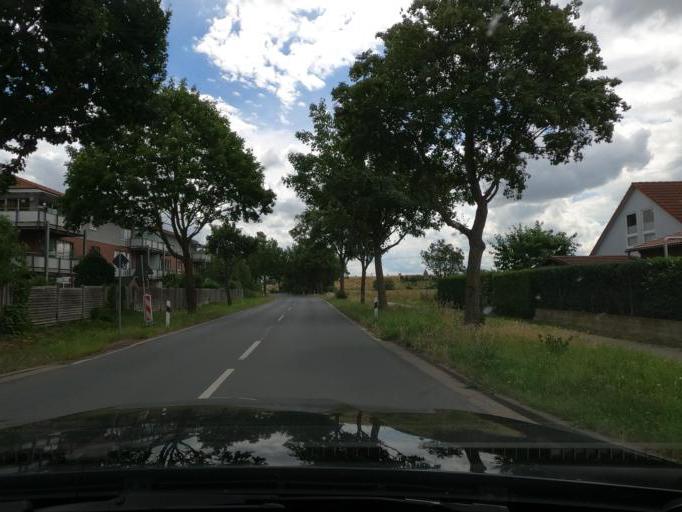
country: DE
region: Lower Saxony
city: Sehnde
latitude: 52.3487
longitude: 9.8994
